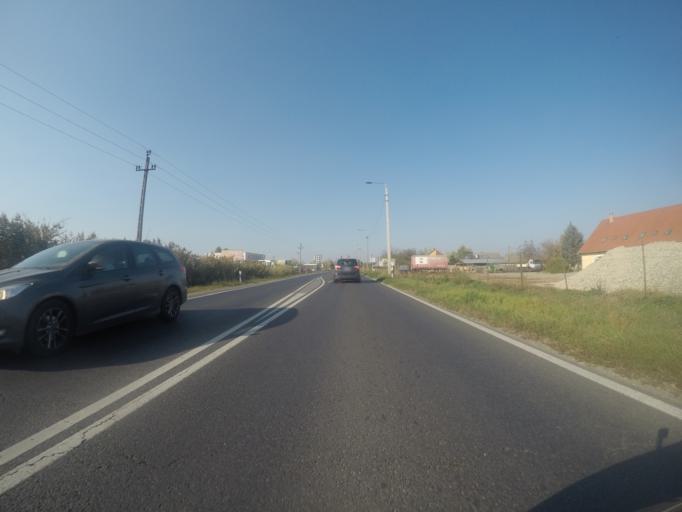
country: HU
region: Tolna
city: Dunafoldvar
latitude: 46.8077
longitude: 18.9134
